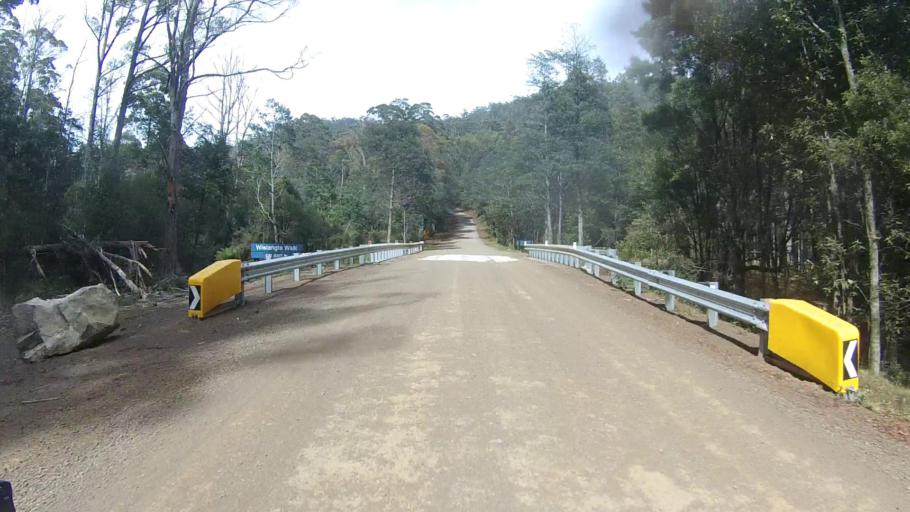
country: AU
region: Tasmania
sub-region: Sorell
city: Sorell
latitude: -42.6925
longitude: 147.8626
